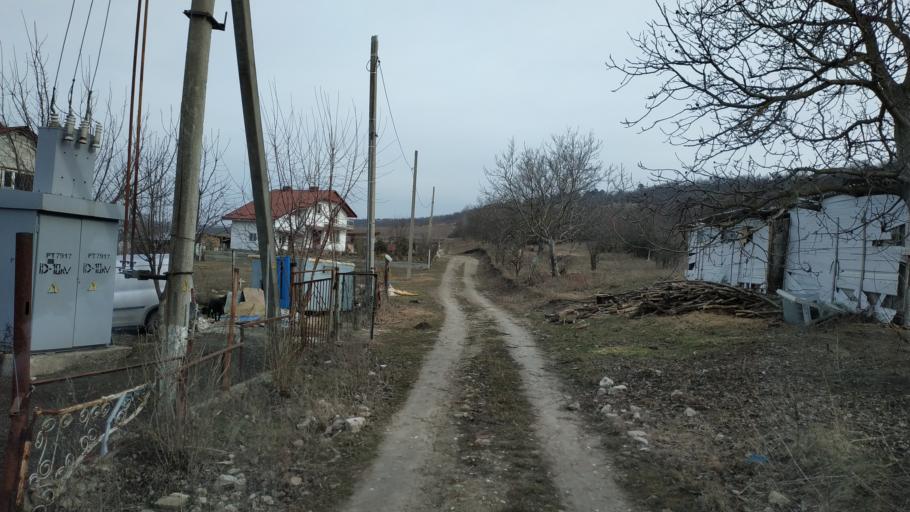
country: MD
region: Chisinau
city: Vatra
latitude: 47.0989
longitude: 28.7372
